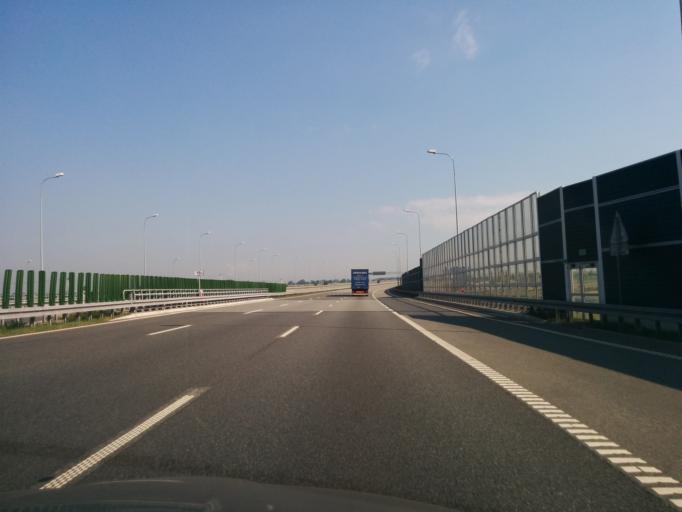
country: PL
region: Silesian Voivodeship
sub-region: Powiat tarnogorski
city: Wieszowa
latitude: 50.3471
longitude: 18.7247
